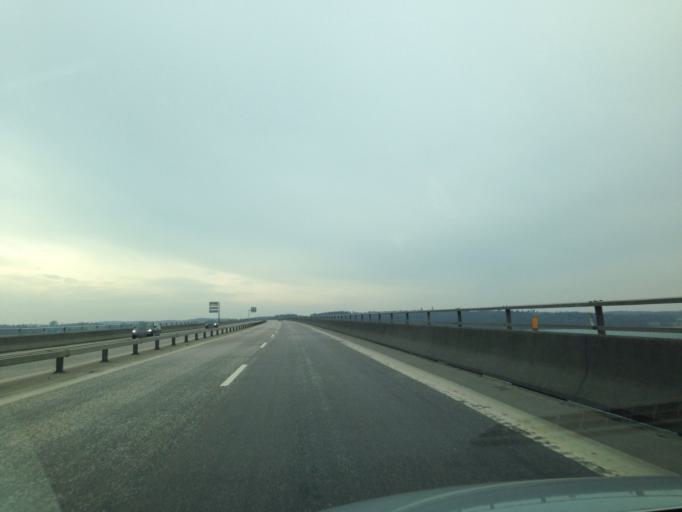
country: DK
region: Zealand
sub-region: Vordingborg Kommune
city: Nyrad
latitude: 54.9575
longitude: 11.9937
